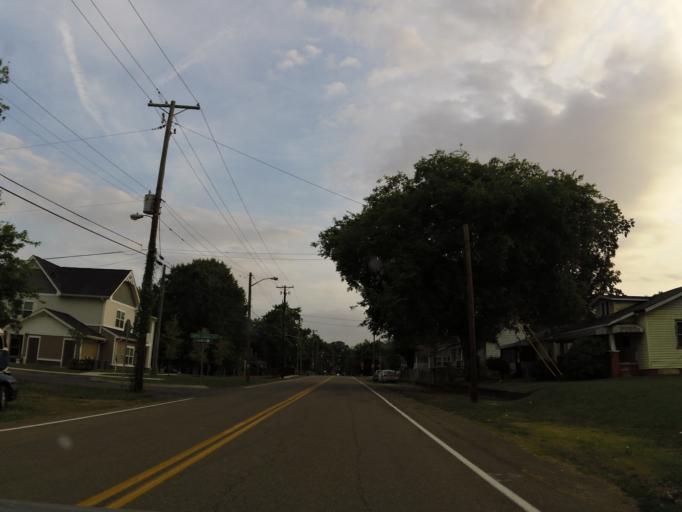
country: US
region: Tennessee
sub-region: Knox County
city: Knoxville
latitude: 35.9824
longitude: -83.8909
